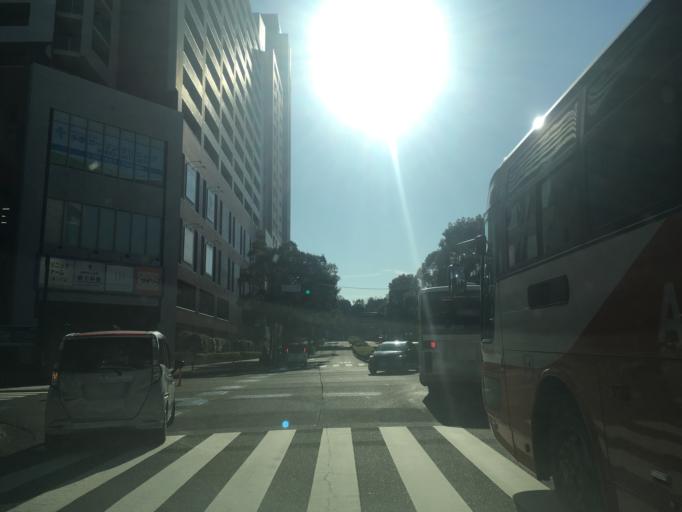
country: JP
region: Tokyo
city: Hino
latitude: 35.6247
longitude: 139.4263
